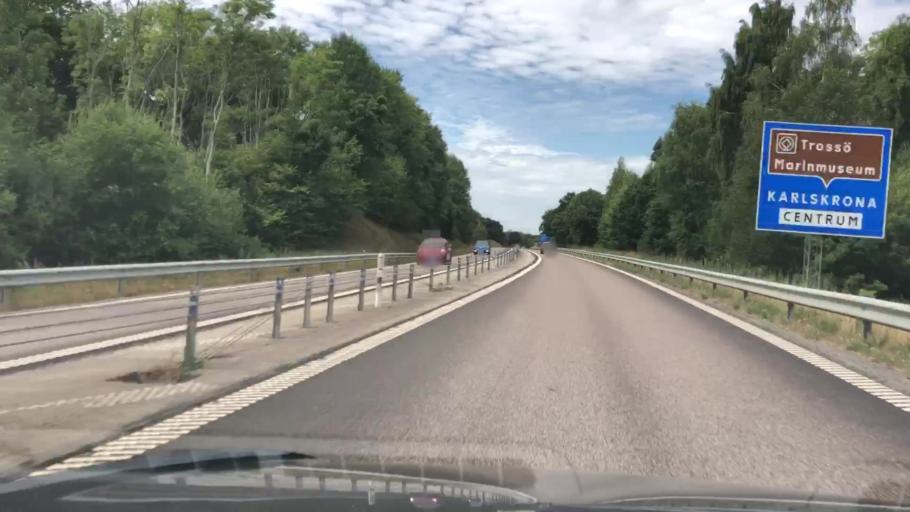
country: SE
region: Blekinge
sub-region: Karlskrona Kommun
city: Rodeby
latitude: 56.2027
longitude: 15.6658
